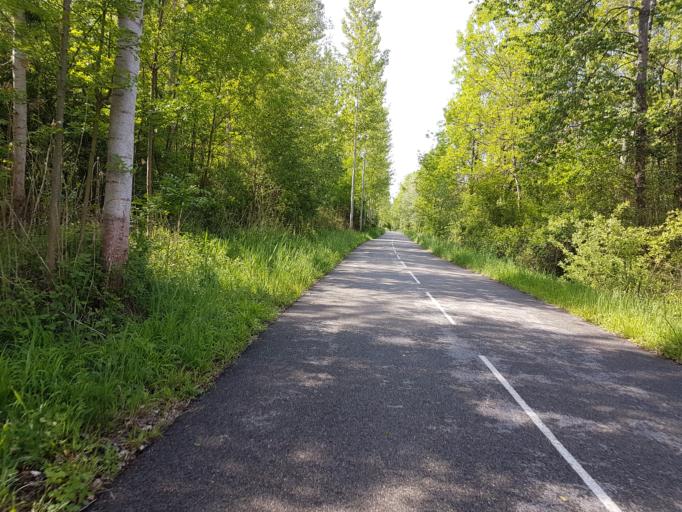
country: FR
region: Rhone-Alpes
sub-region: Departement de l'Ain
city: Culoz
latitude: 45.8576
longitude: 5.8219
